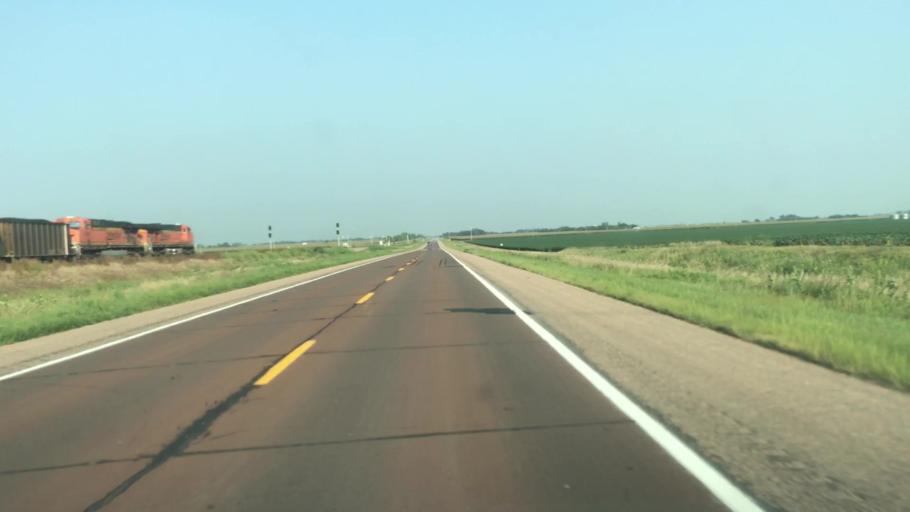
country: US
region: Nebraska
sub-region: Hall County
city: Wood River
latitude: 40.9958
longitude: -98.5785
